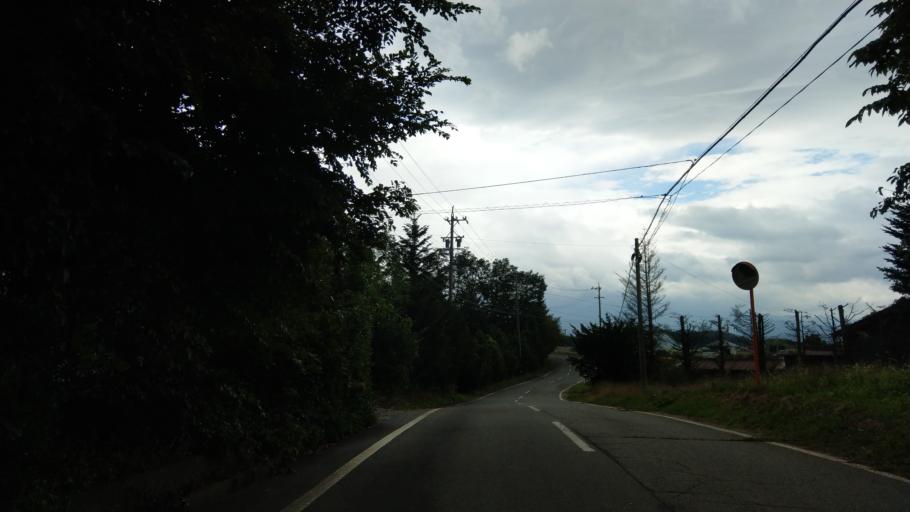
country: JP
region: Nagano
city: Komoro
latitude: 36.3024
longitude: 138.3869
